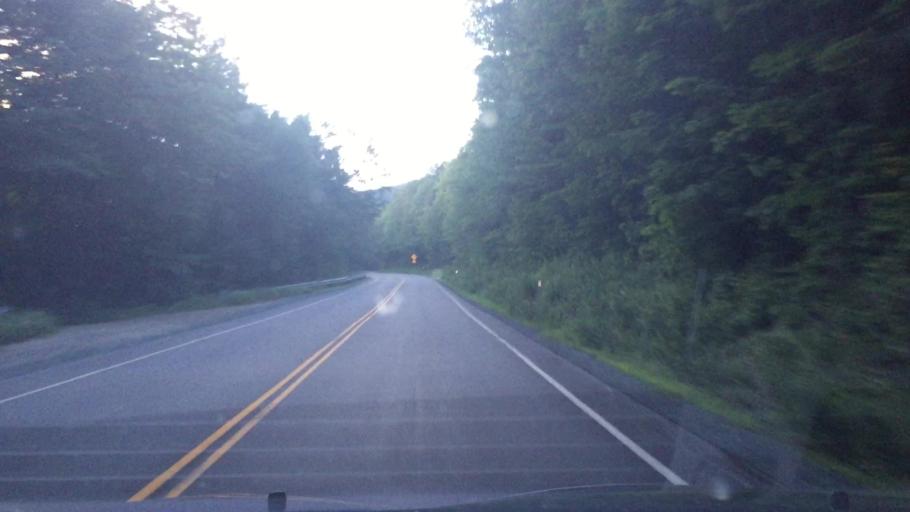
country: US
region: New Hampshire
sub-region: Grafton County
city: Woodstock
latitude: 44.0360
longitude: -71.5205
